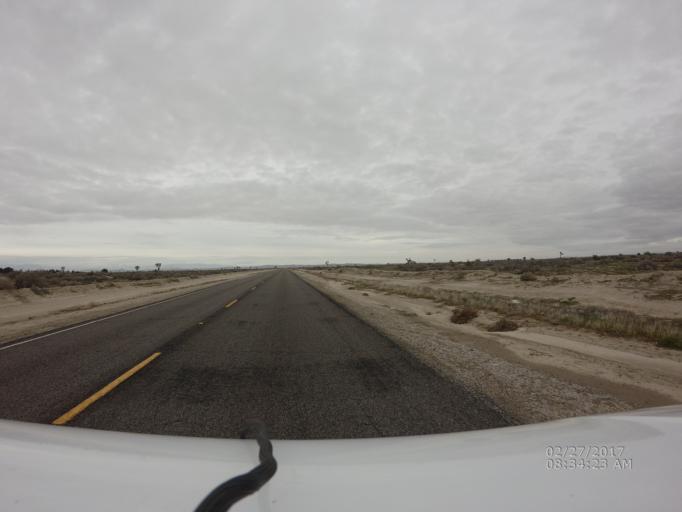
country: US
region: California
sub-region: Los Angeles County
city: Lancaster
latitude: 34.7129
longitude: -118.0592
